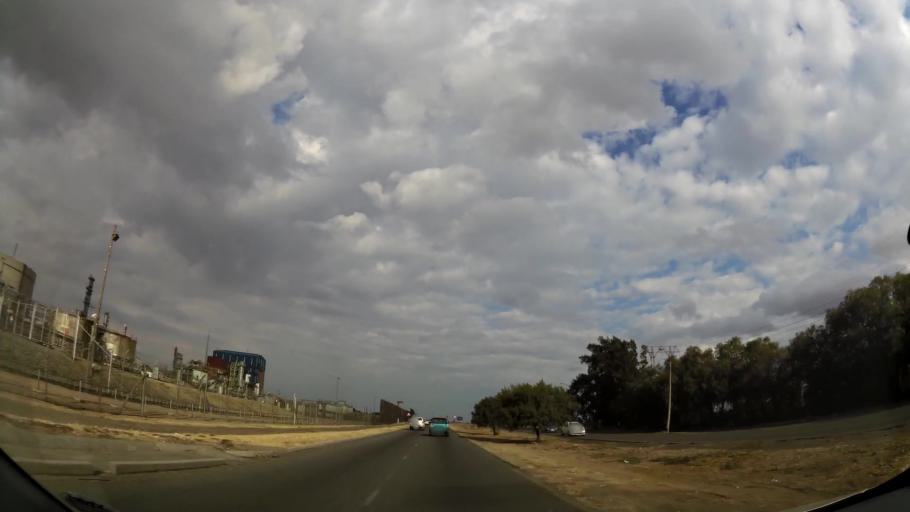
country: ZA
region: Orange Free State
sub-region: Fezile Dabi District Municipality
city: Sasolburg
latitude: -26.8299
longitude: 27.8400
